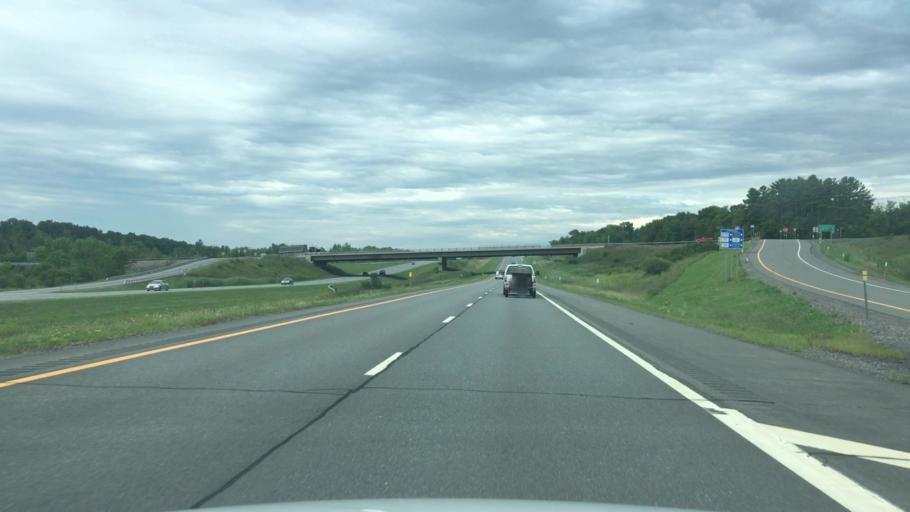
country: US
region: New York
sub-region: Albany County
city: Altamont
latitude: 42.7608
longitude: -74.1174
